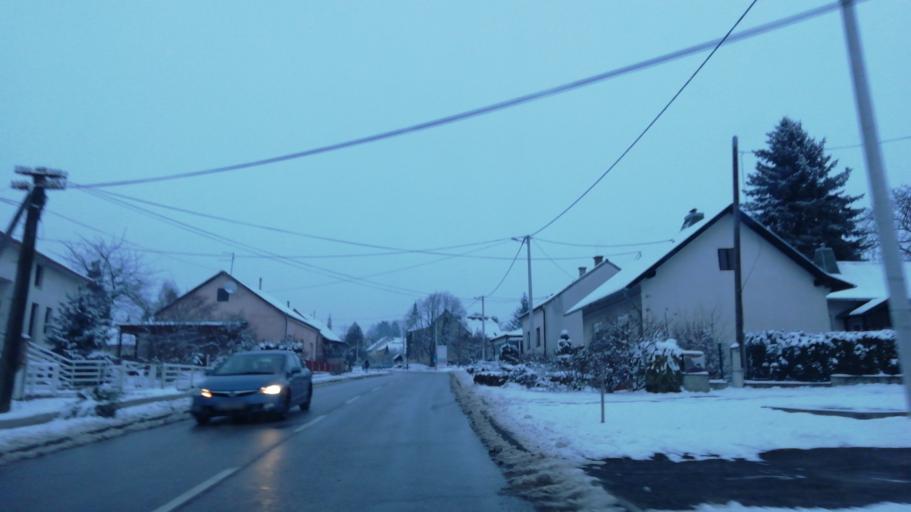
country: HR
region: Zagrebacka
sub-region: Grad Vrbovec
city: Vrbovec
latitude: 45.8808
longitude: 16.4140
